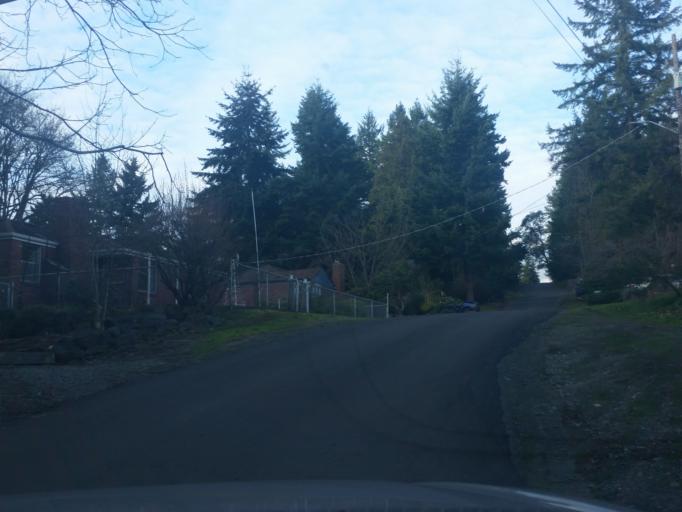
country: US
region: Washington
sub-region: King County
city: Lake Forest Park
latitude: 47.7041
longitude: -122.3097
